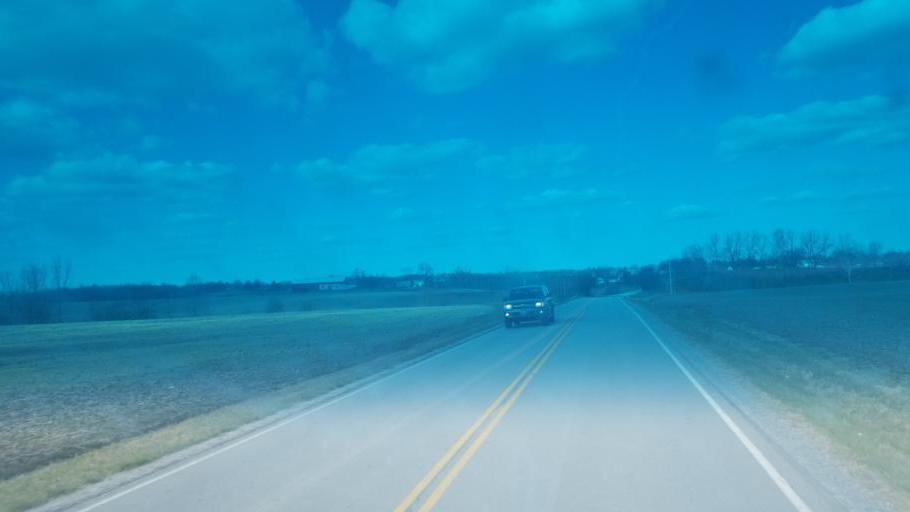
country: US
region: Ohio
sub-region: Highland County
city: Greenfield
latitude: 39.3336
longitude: -83.4071
